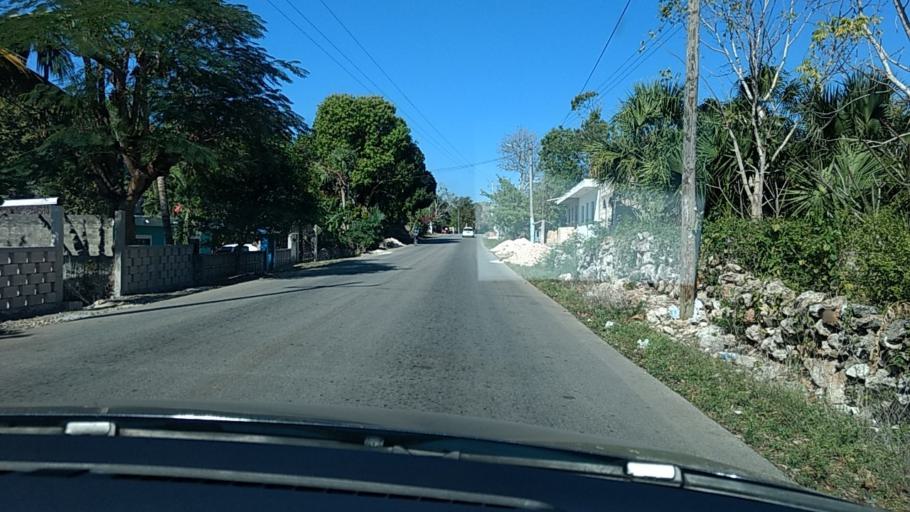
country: MX
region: Yucatan
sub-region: Uayma
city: Uayma
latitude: 20.7134
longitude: -88.2636
